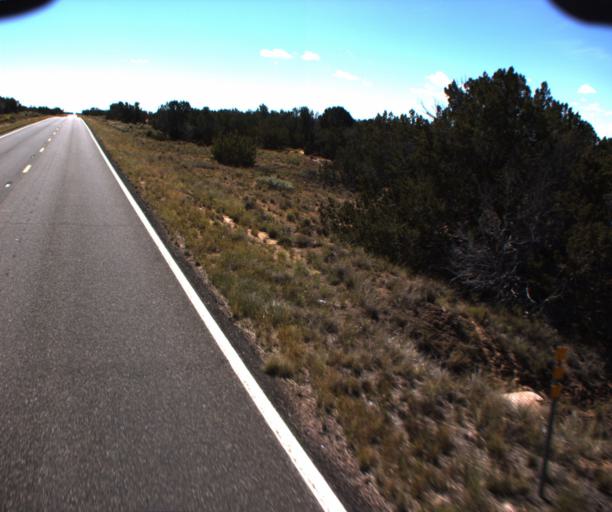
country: US
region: Arizona
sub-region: Apache County
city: Houck
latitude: 34.8899
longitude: -109.2380
